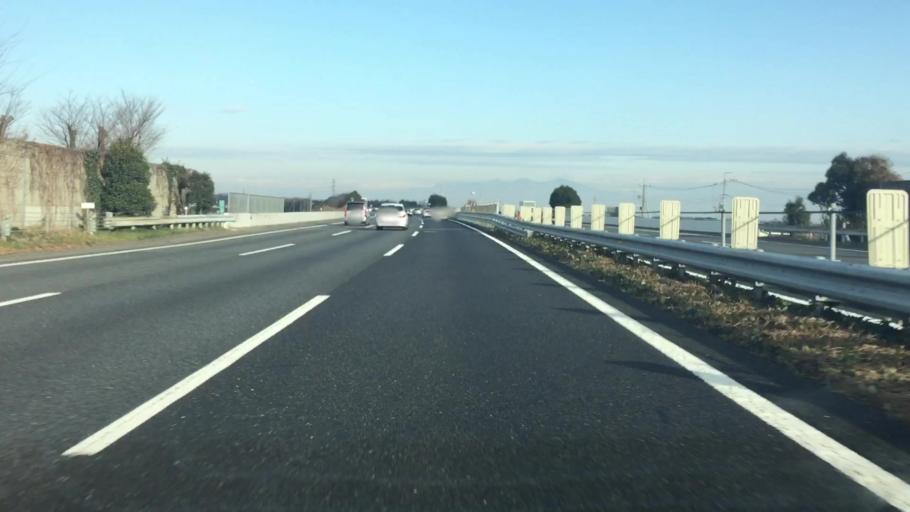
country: JP
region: Saitama
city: Honjo
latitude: 36.1868
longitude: 139.1905
